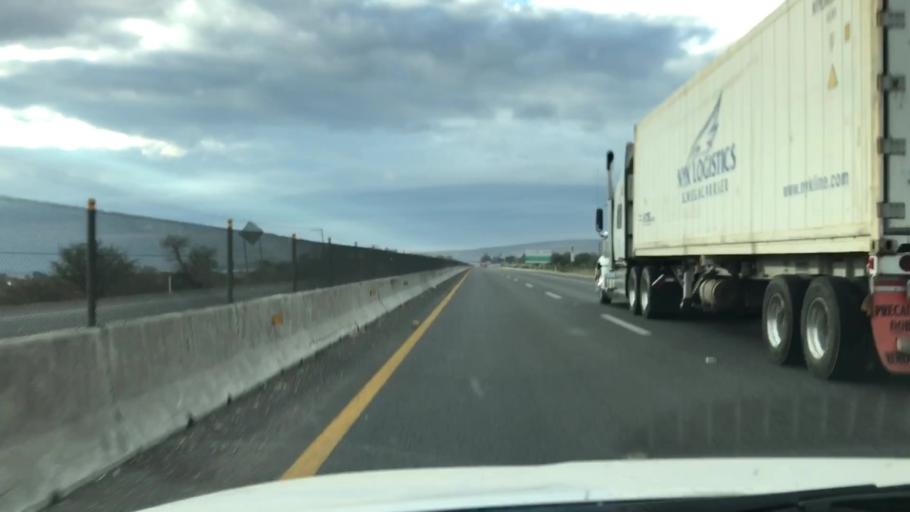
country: MX
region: Guanajuato
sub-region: Penjamo
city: Mezquite de Luna
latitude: 20.3851
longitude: -101.9078
